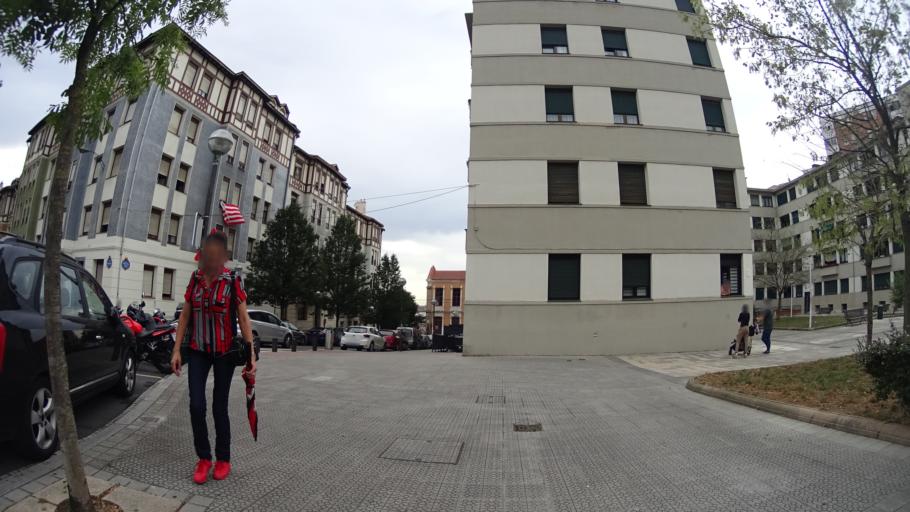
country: ES
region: Basque Country
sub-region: Bizkaia
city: Santutxu
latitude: 43.2566
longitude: -2.9200
